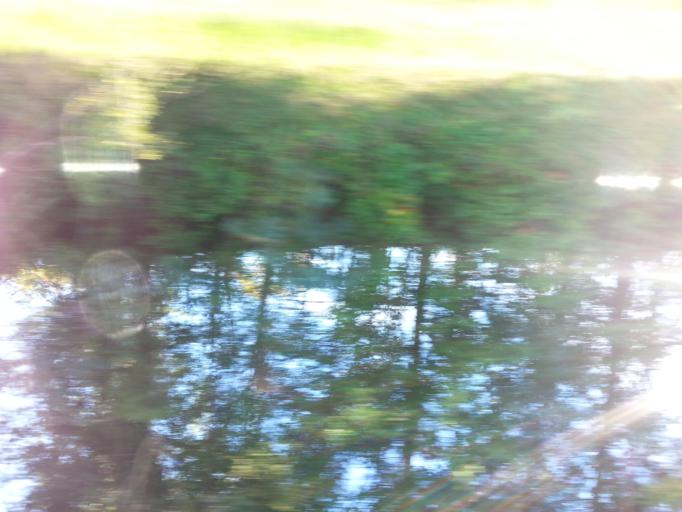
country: US
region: Alabama
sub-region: Lauderdale County
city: Killen
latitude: 34.8583
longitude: -87.5353
